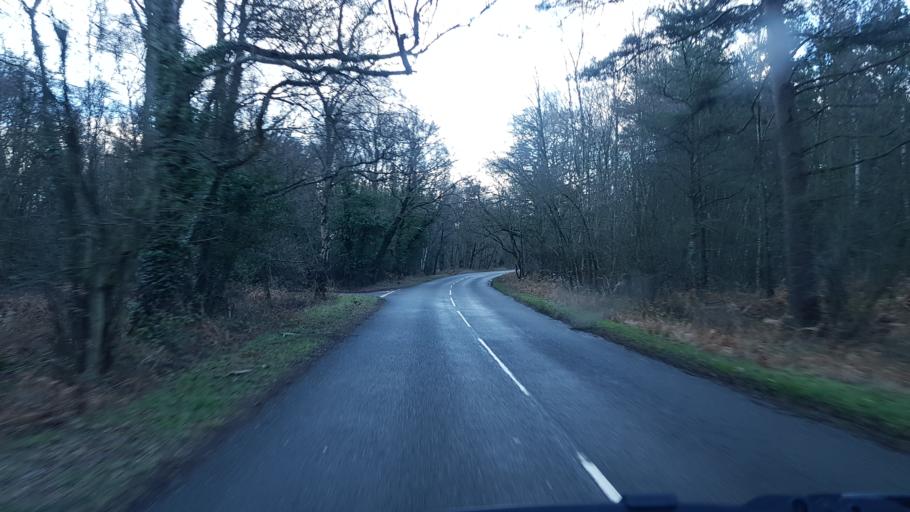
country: GB
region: England
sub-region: Surrey
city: Elstead
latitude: 51.2032
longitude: -0.7028
